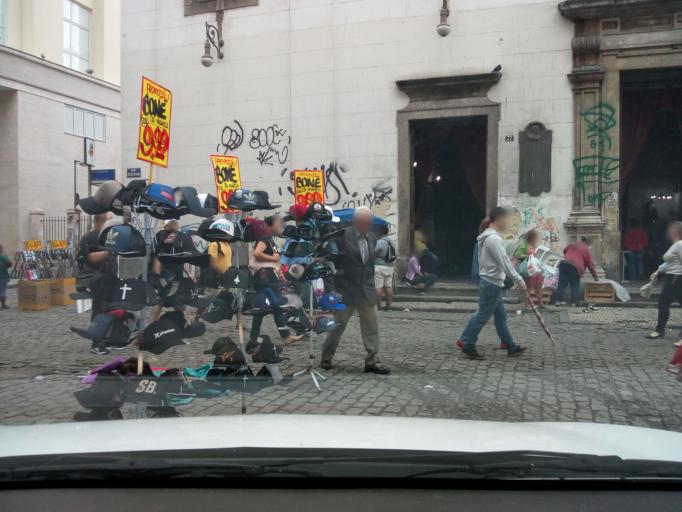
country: BR
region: Rio de Janeiro
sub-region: Rio De Janeiro
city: Rio de Janeiro
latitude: -22.9041
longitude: -43.1801
